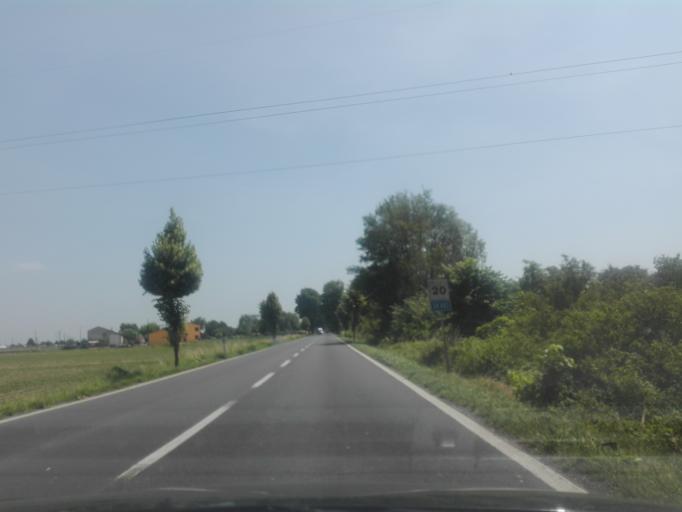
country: IT
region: Veneto
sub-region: Provincia di Rovigo
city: Adria
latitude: 45.0612
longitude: 12.0342
